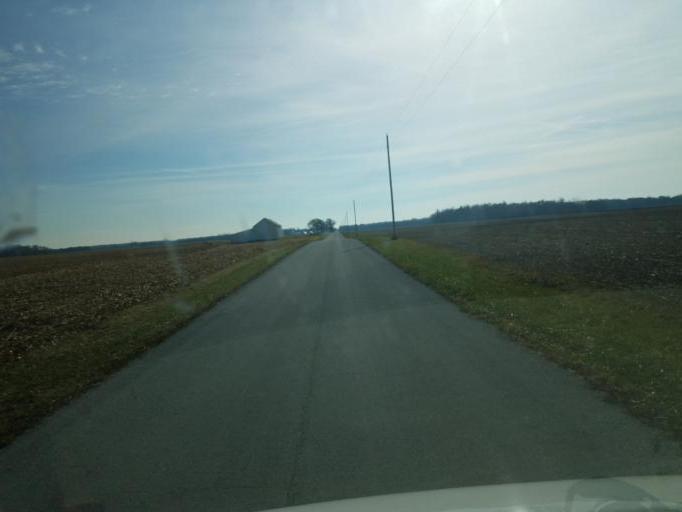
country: US
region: Ohio
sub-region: Hardin County
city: Forest
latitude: 40.6699
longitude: -83.4398
